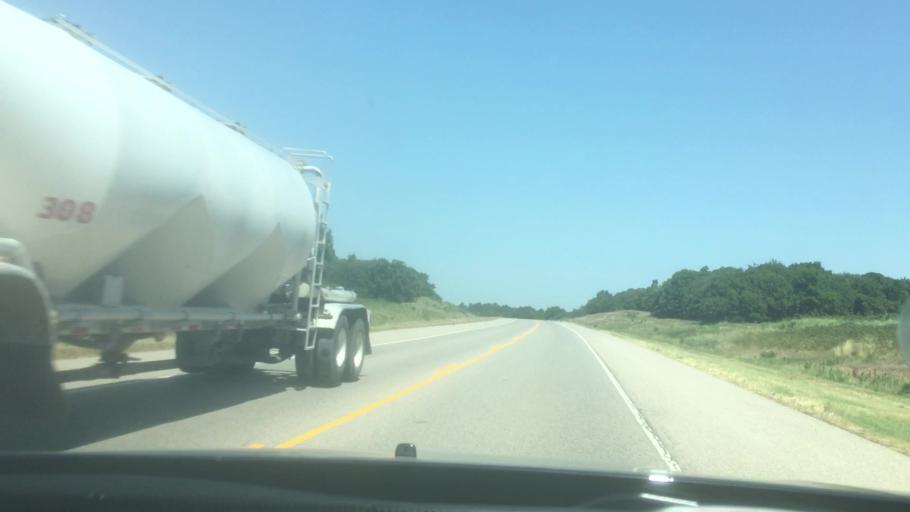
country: US
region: Oklahoma
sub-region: Pontotoc County
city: Ada
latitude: 34.6741
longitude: -96.5726
